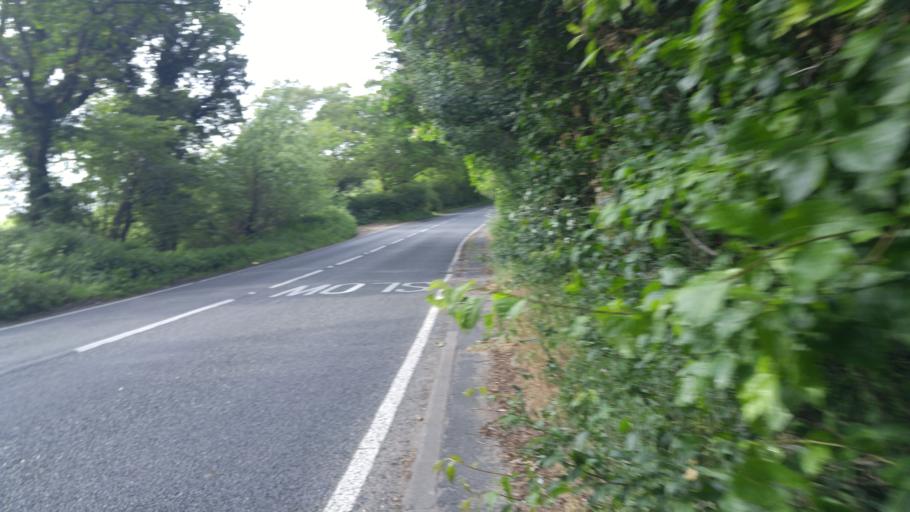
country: GB
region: England
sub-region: Essex
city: Layer de la Haye
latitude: 51.8528
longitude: 0.8669
